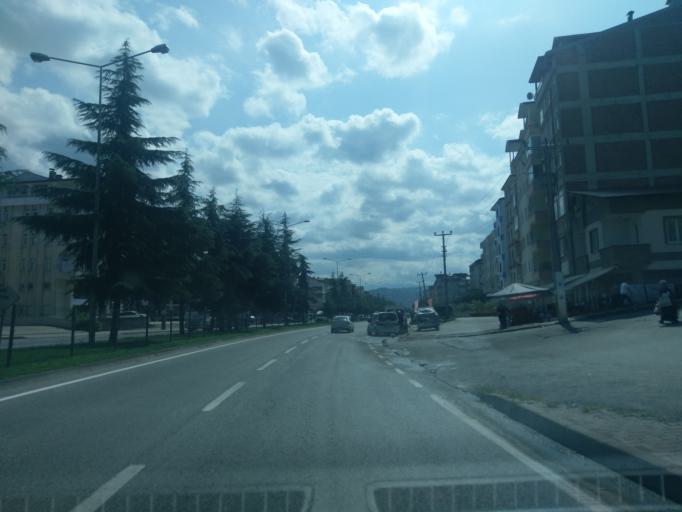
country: TR
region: Ordu
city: Ordu
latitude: 40.9652
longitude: 37.9001
